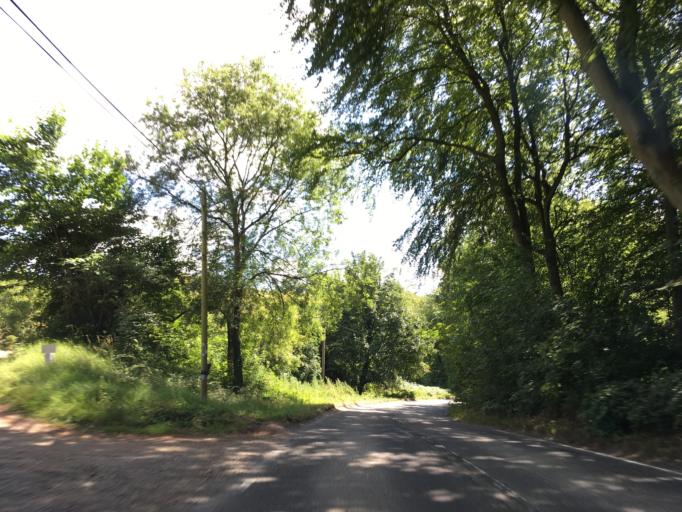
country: GB
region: England
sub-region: Gloucestershire
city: Painswick
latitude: 51.8086
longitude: -2.1968
